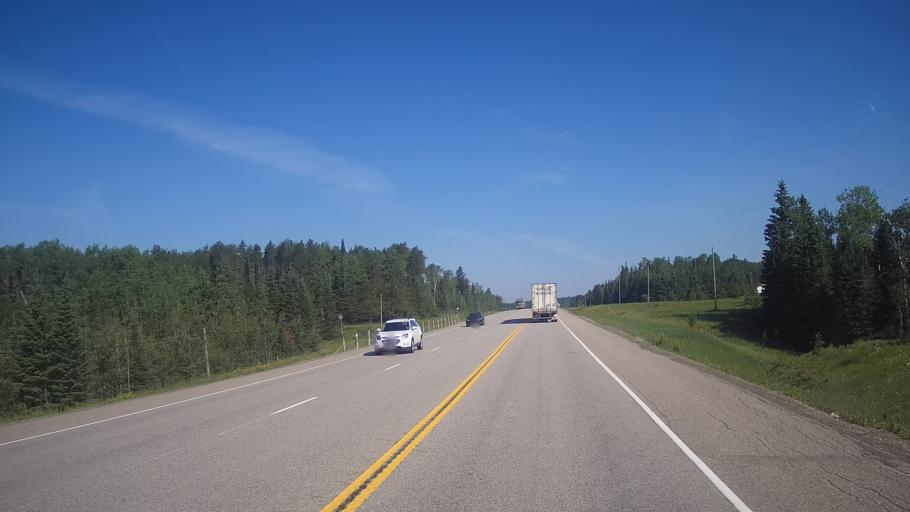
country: CA
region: Ontario
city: Dryden
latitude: 49.7089
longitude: -92.5871
